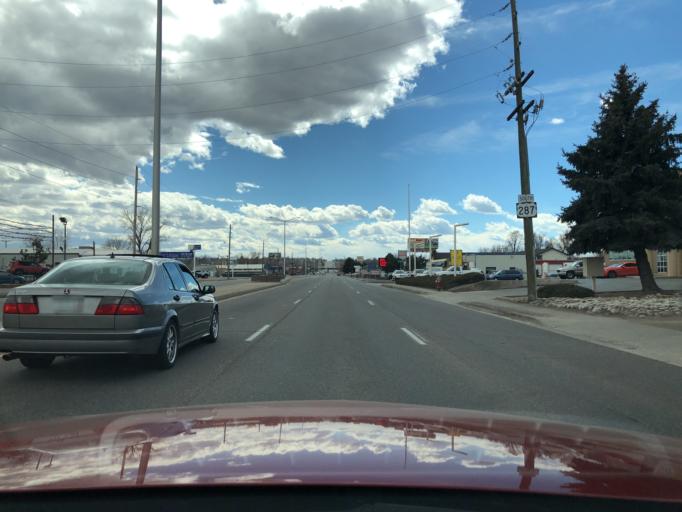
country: US
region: Colorado
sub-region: Adams County
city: Berkley
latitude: 39.8114
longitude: -105.0254
